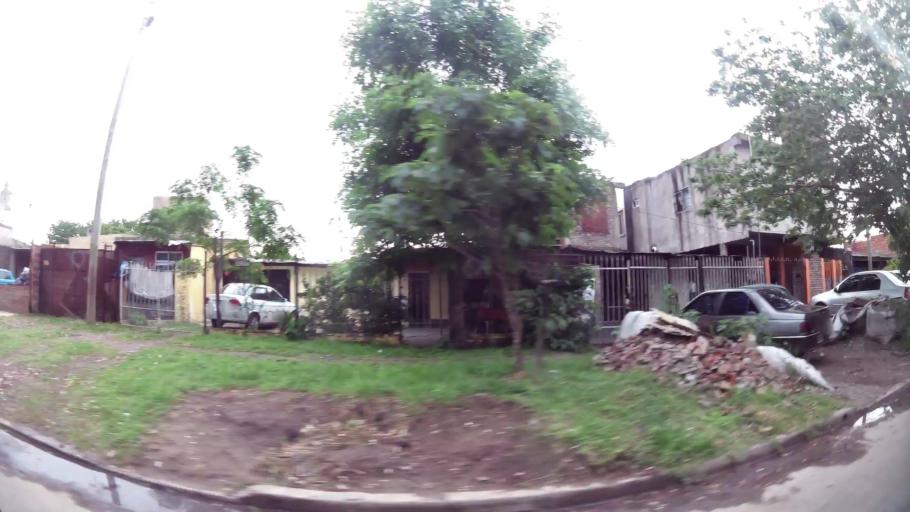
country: AR
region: Buenos Aires
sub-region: Partido de Lanus
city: Lanus
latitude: -34.7255
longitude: -58.3475
